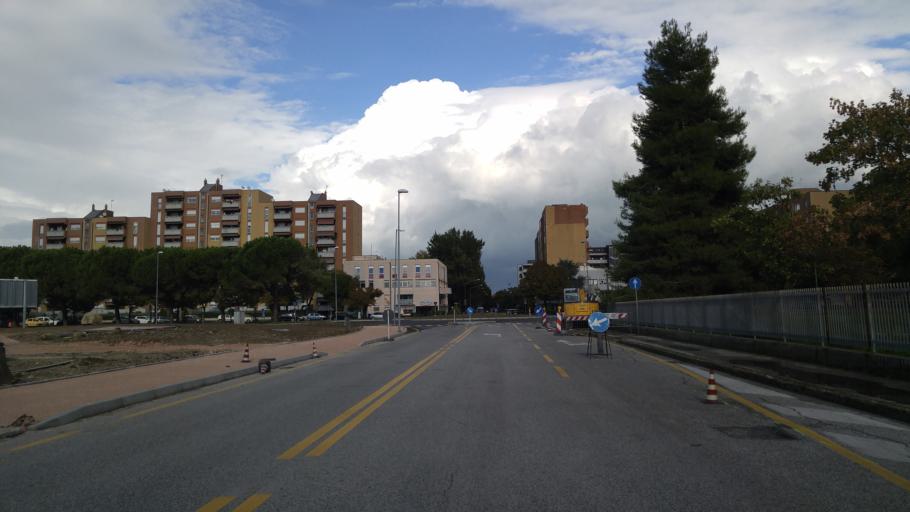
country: IT
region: The Marches
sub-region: Provincia di Pesaro e Urbino
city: Pesaro
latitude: 43.8947
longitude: 12.8974
